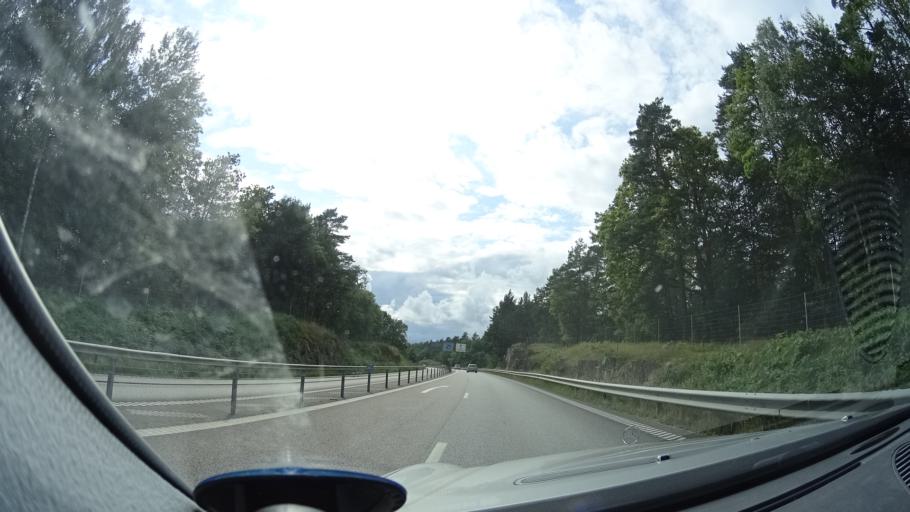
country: SE
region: Blekinge
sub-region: Karlshamns Kommun
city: Morrum
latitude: 56.1901
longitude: 14.7998
